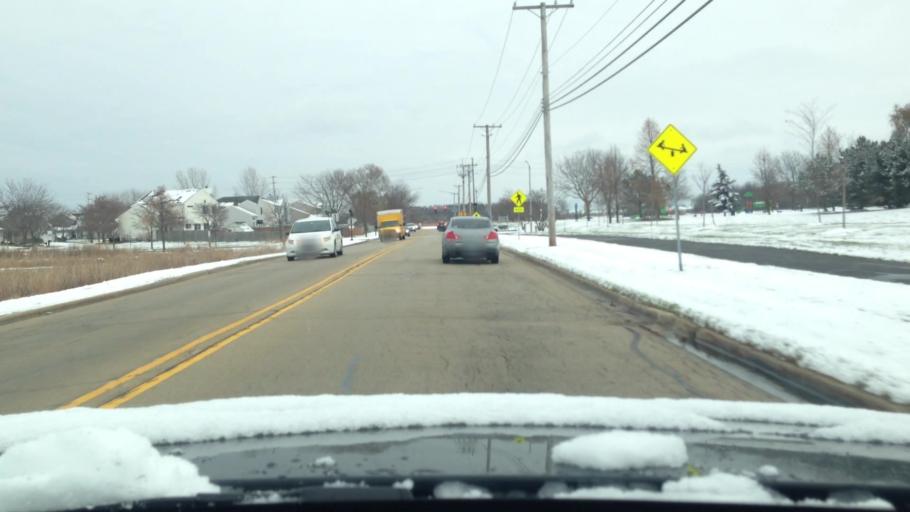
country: US
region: Illinois
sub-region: McHenry County
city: Huntley
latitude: 42.1829
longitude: -88.3875
